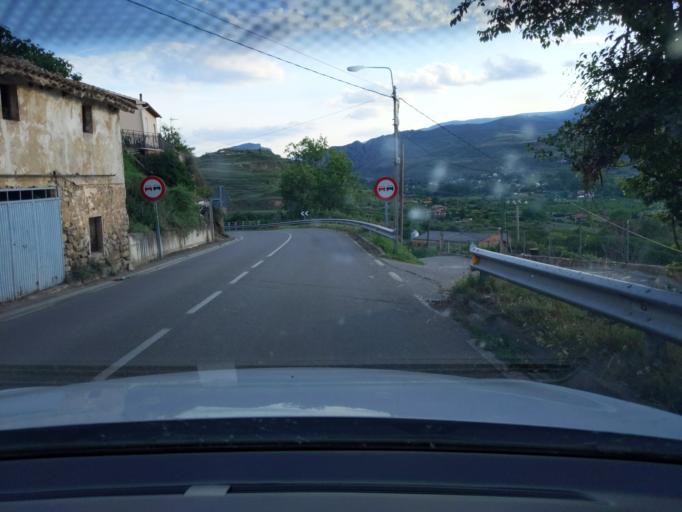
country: ES
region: La Rioja
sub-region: Provincia de La Rioja
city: Nalda
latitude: 42.3355
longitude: -2.4899
